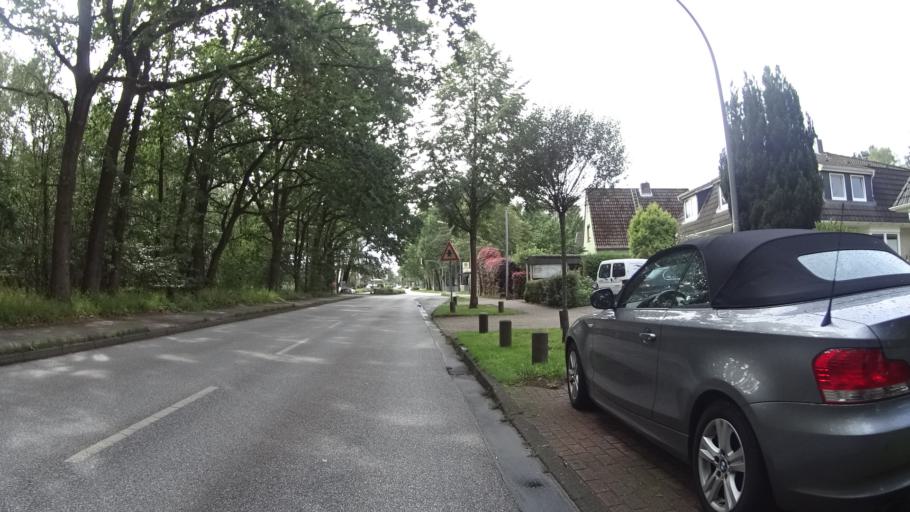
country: DE
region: Schleswig-Holstein
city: Henstedt-Ulzburg
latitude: 53.7605
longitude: 9.9970
